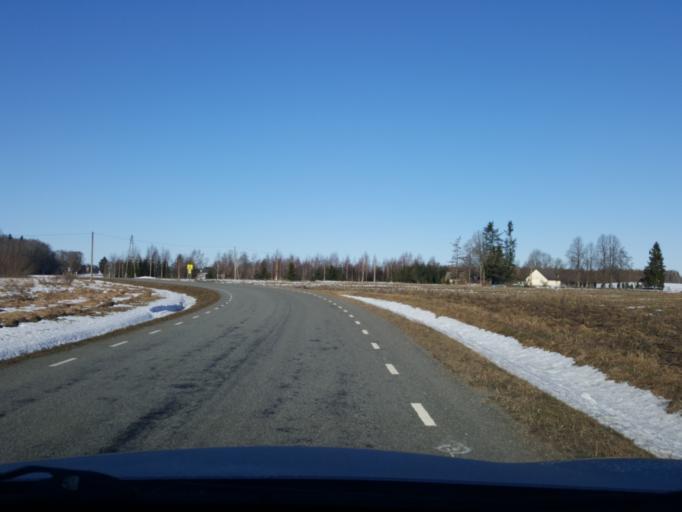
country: EE
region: Viljandimaa
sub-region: Viljandi linn
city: Viljandi
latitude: 58.4066
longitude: 25.5684
